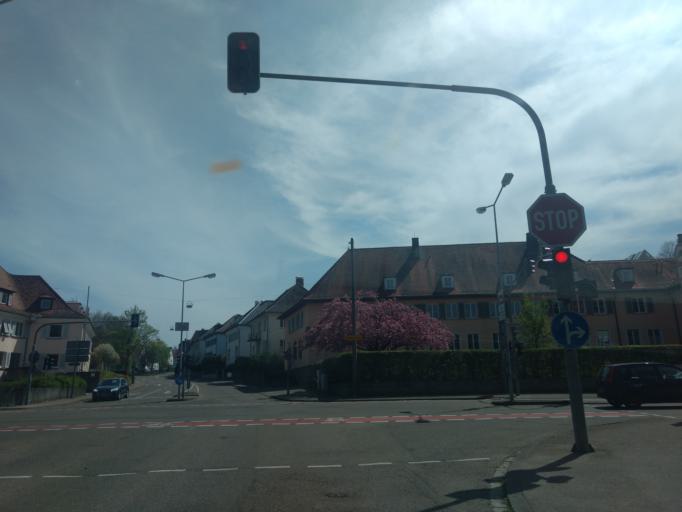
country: DE
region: Baden-Wuerttemberg
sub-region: Regierungsbezirk Stuttgart
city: Schwabisch Gmund
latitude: 48.7953
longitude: 9.7907
